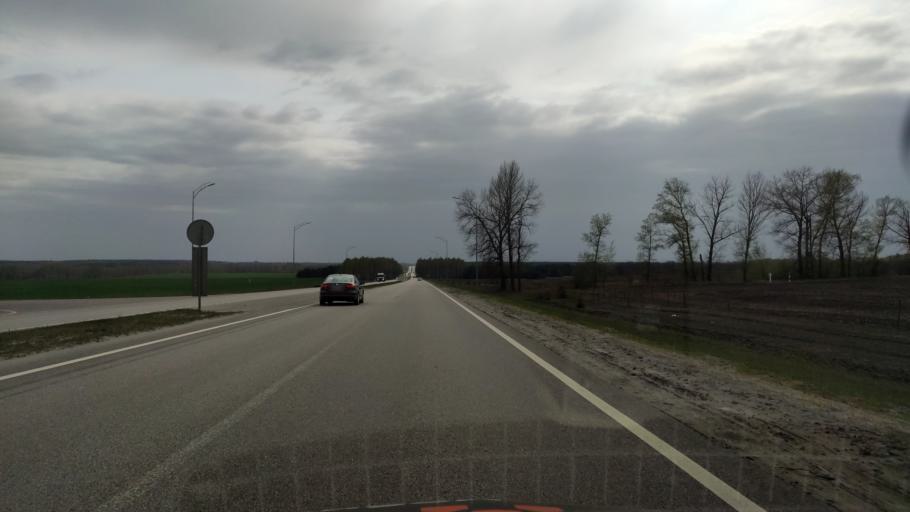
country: RU
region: Belgorod
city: Staryy Oskol
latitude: 51.4171
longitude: 37.8884
